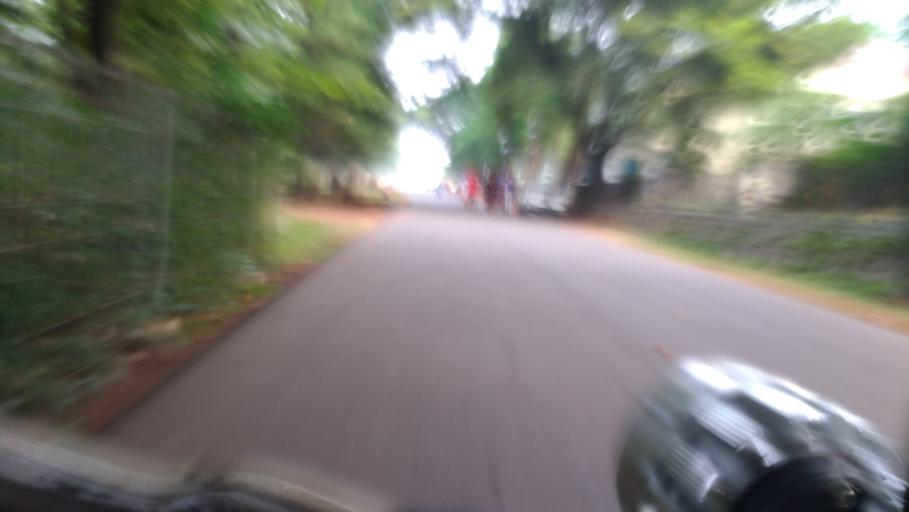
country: ID
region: West Java
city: Cileungsir
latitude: -6.3694
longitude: 106.8993
